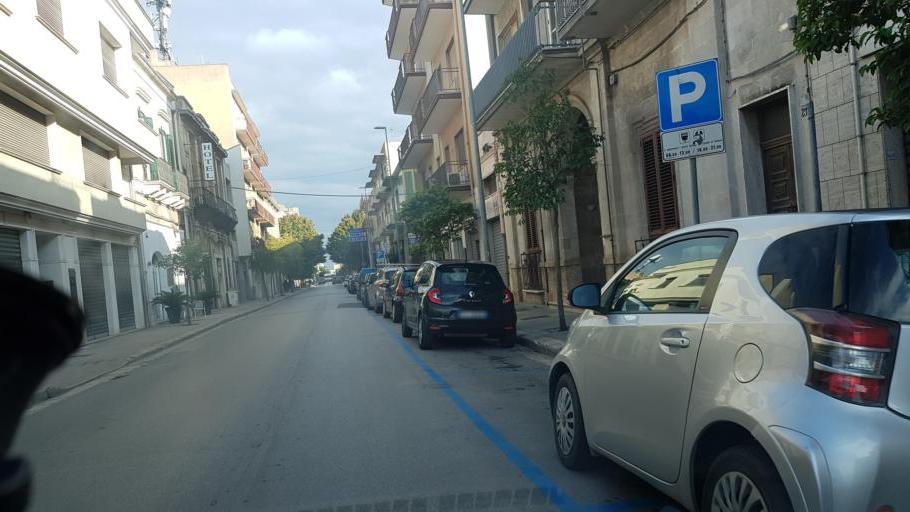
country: IT
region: Apulia
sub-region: Provincia di Brindisi
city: Francavilla Fontana
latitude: 40.5275
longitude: 17.5818
